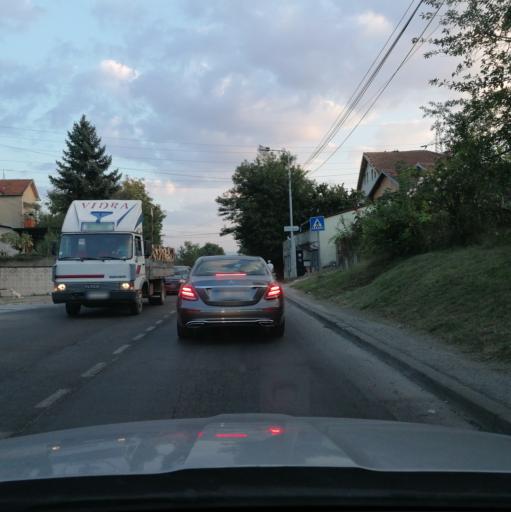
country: RS
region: Central Serbia
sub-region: Raski Okrug
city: Kraljevo
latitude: 43.7340
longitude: 20.6804
